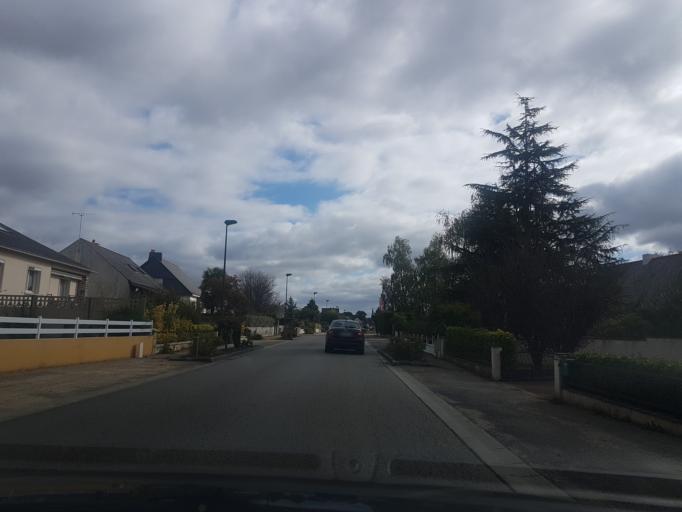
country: FR
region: Pays de la Loire
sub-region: Departement de la Loire-Atlantique
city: Ligne
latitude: 47.4131
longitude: -1.3858
